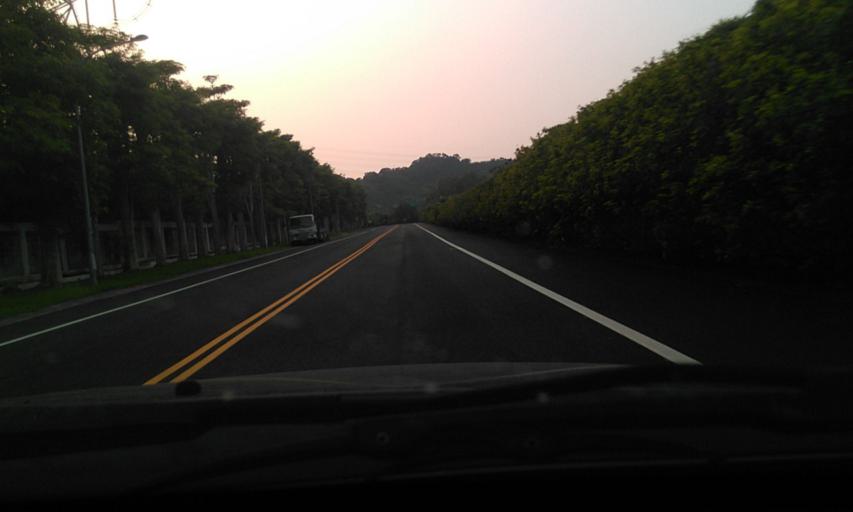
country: TW
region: Taiwan
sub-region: Hsinchu
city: Hsinchu
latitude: 24.6941
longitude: 120.9871
